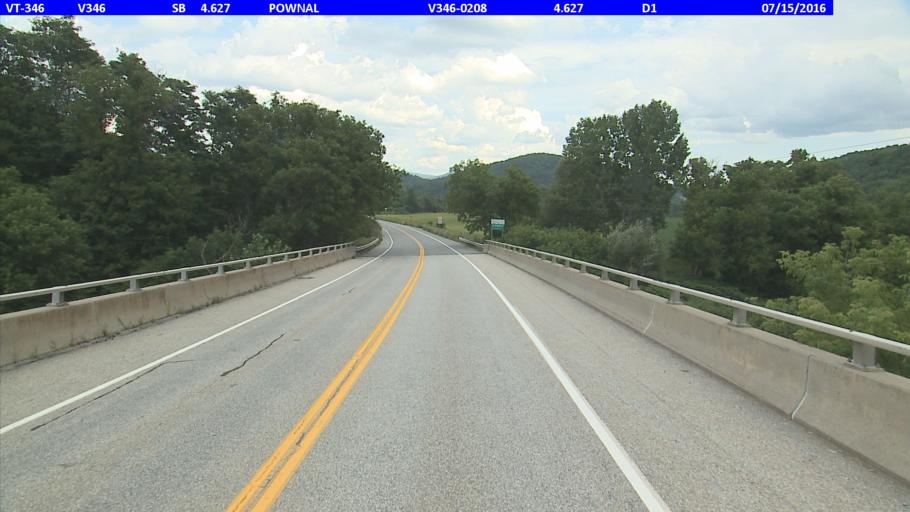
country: US
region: New York
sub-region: Rensselaer County
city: Hoosick Falls
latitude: 42.8094
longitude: -73.2864
